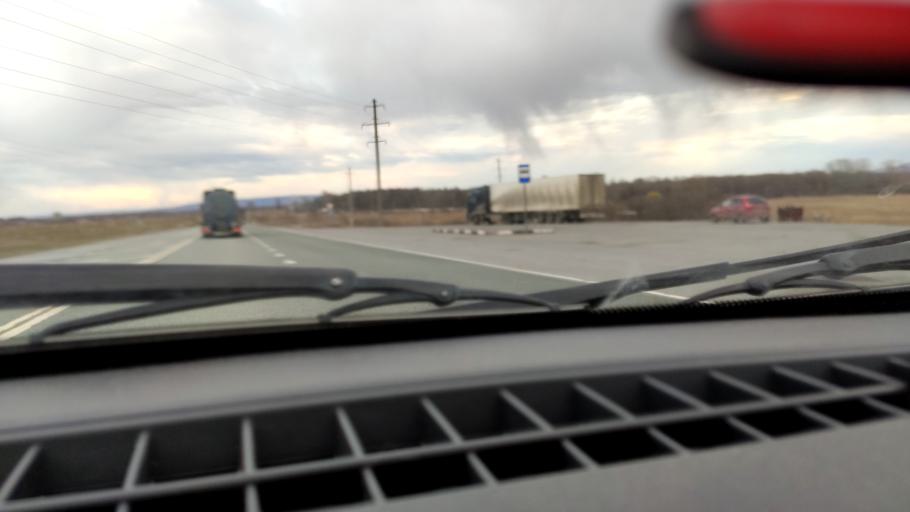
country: RU
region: Bashkortostan
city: Kudeyevskiy
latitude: 54.8168
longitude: 56.7371
